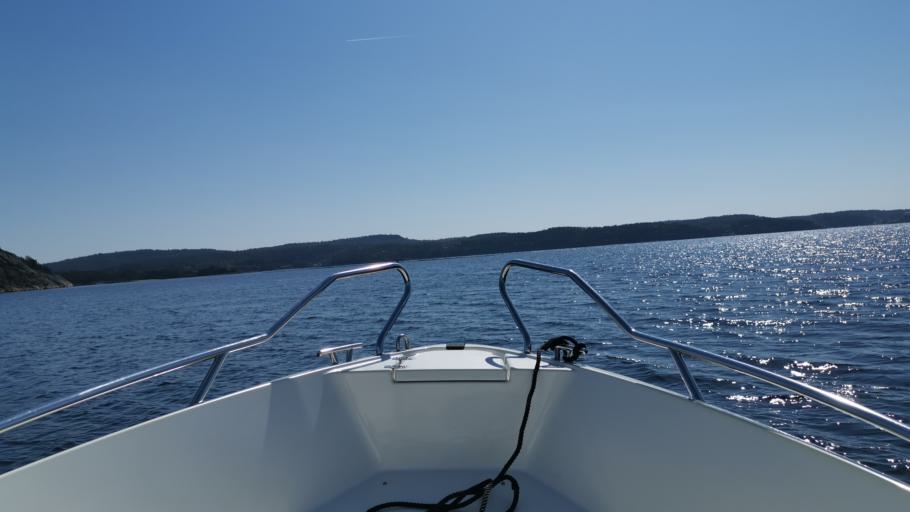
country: SE
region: Vaestra Goetaland
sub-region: Orust
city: Henan
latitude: 58.2495
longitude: 11.5767
